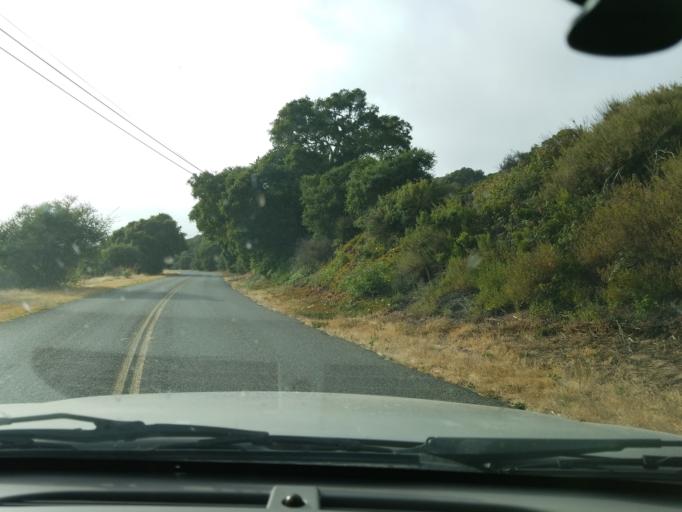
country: US
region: California
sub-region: Monterey County
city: Elkhorn
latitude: 36.8415
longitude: -121.7393
